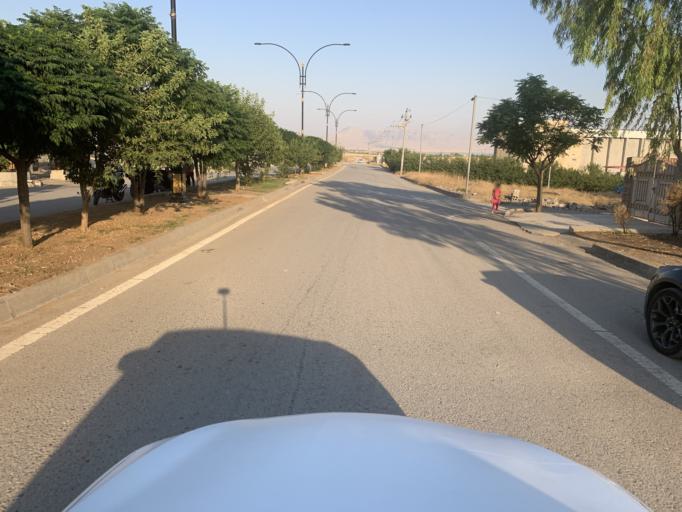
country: IQ
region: As Sulaymaniyah
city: Raniye
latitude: 36.2380
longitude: 44.8803
